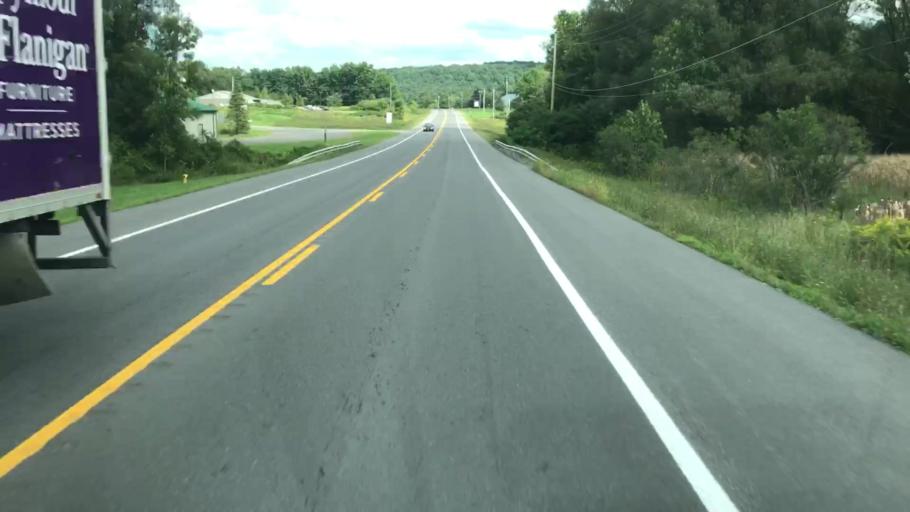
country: US
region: New York
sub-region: Onondaga County
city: Marcellus
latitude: 42.9521
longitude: -76.3504
